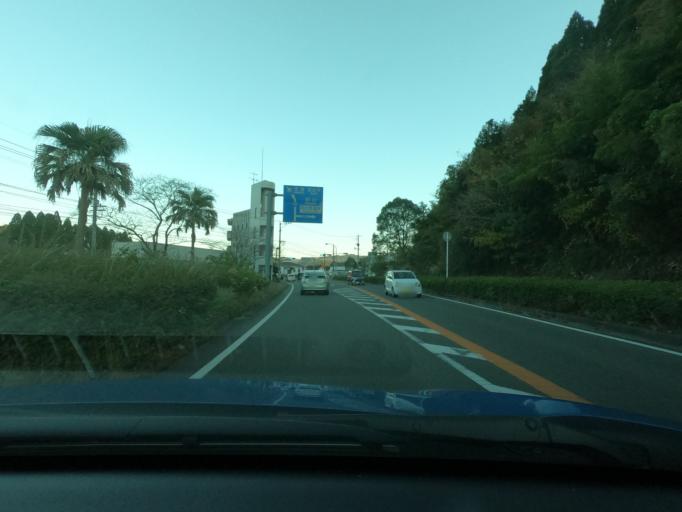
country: JP
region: Kagoshima
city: Satsumasendai
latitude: 31.7968
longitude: 130.4042
